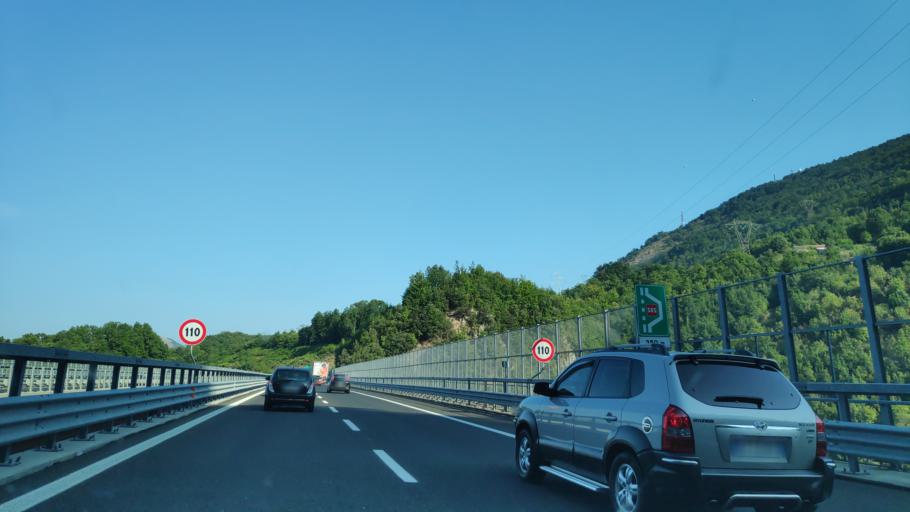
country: IT
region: Basilicate
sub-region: Provincia di Potenza
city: Lagonegro
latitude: 40.1268
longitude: 15.7767
